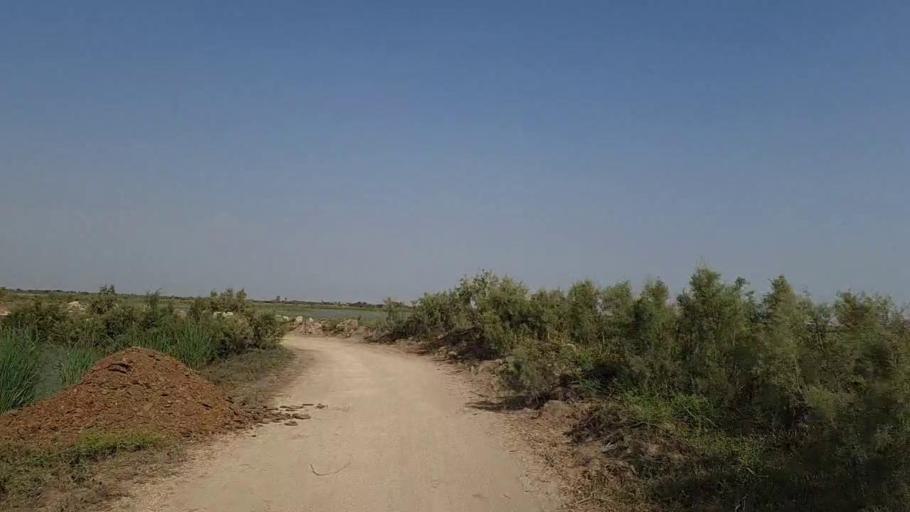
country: PK
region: Sindh
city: Daro Mehar
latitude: 24.7634
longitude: 68.1677
